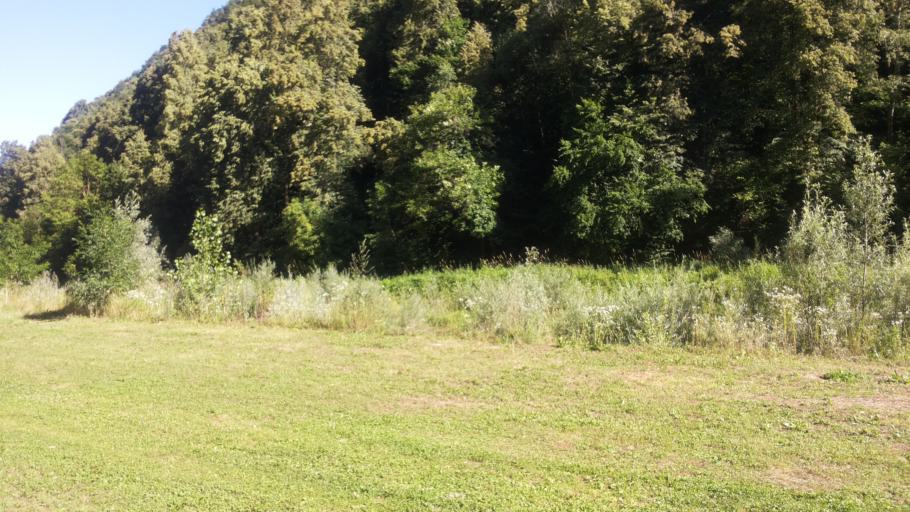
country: IT
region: Piedmont
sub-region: Provincia di Cuneo
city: Frassino
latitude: 44.5703
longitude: 7.2790
